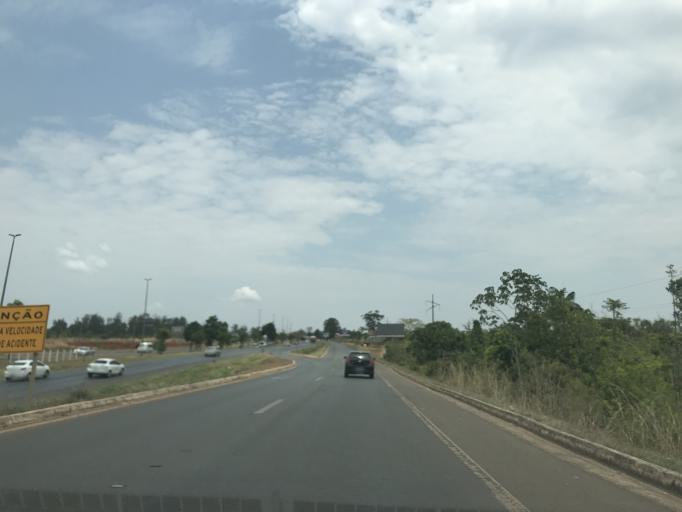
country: BR
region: Federal District
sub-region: Brasilia
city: Brasilia
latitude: -15.6661
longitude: -47.8094
